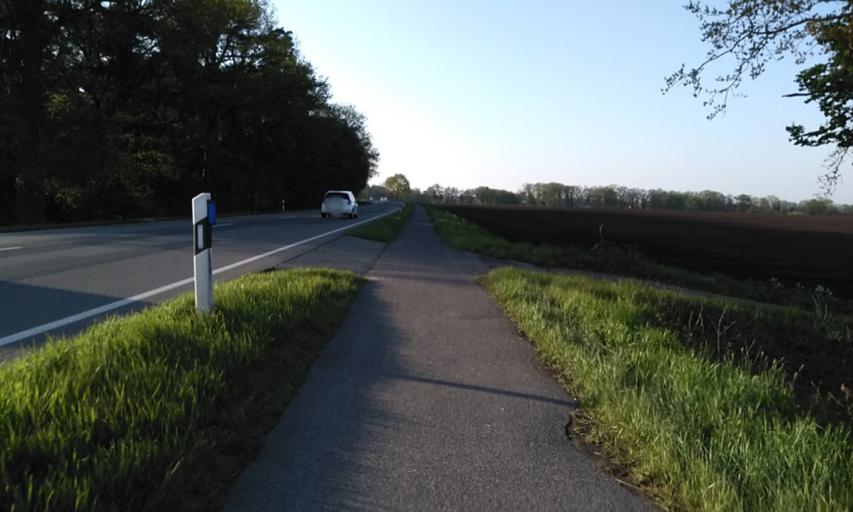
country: DE
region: Lower Saxony
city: Dollern
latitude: 53.5268
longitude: 9.5570
